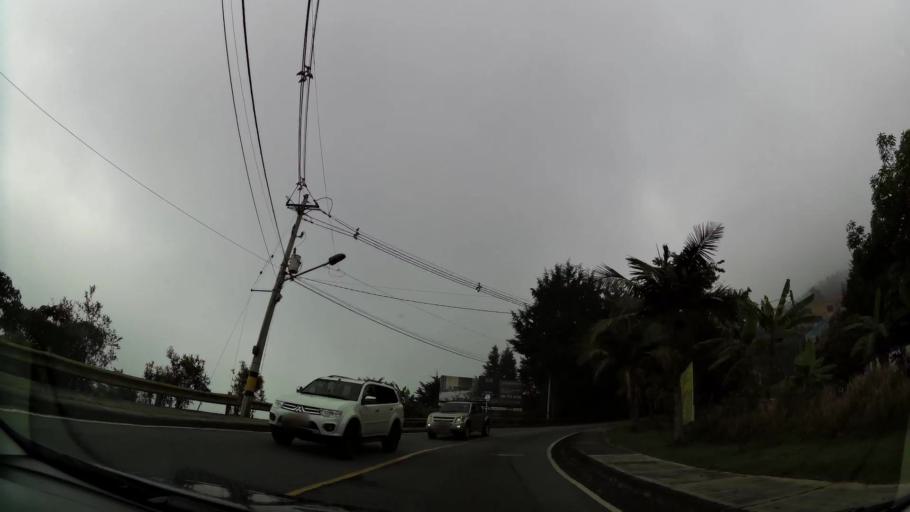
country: CO
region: Antioquia
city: Envigado
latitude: 6.1861
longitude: -75.5488
